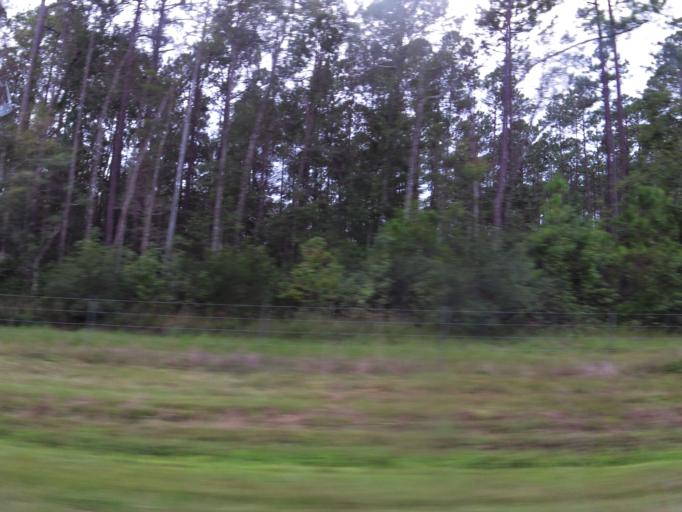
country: US
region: Florida
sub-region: Duval County
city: Baldwin
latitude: 30.3665
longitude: -81.9242
